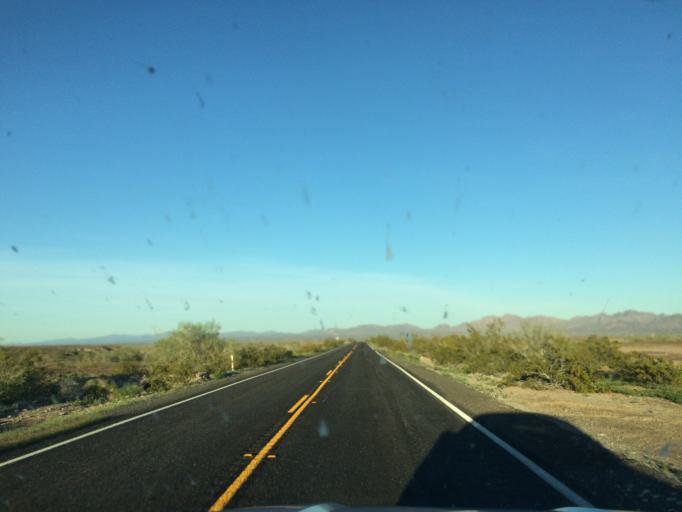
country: US
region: California
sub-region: Riverside County
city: Mesa Verde
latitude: 33.2870
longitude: -114.7657
